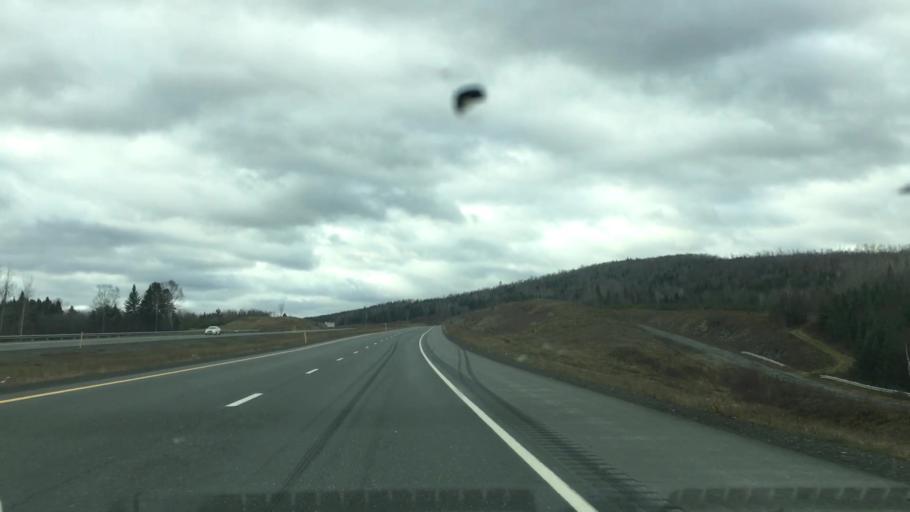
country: US
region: Maine
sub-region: Aroostook County
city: Fort Fairfield
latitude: 46.7318
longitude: -67.7218
